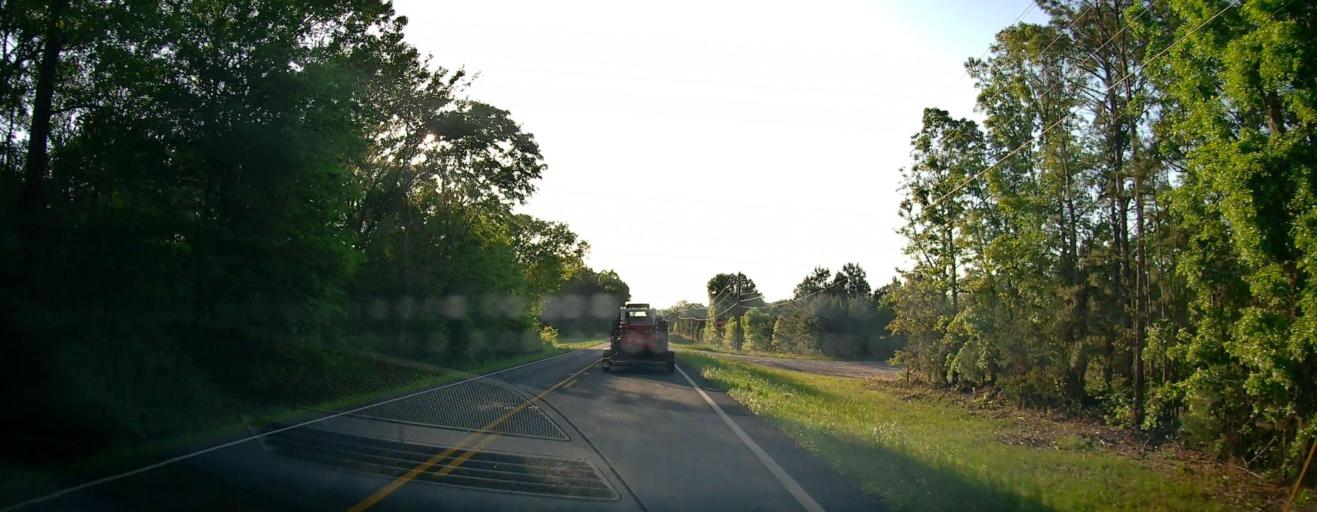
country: US
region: Georgia
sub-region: Walton County
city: Social Circle
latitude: 33.5105
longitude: -83.6827
